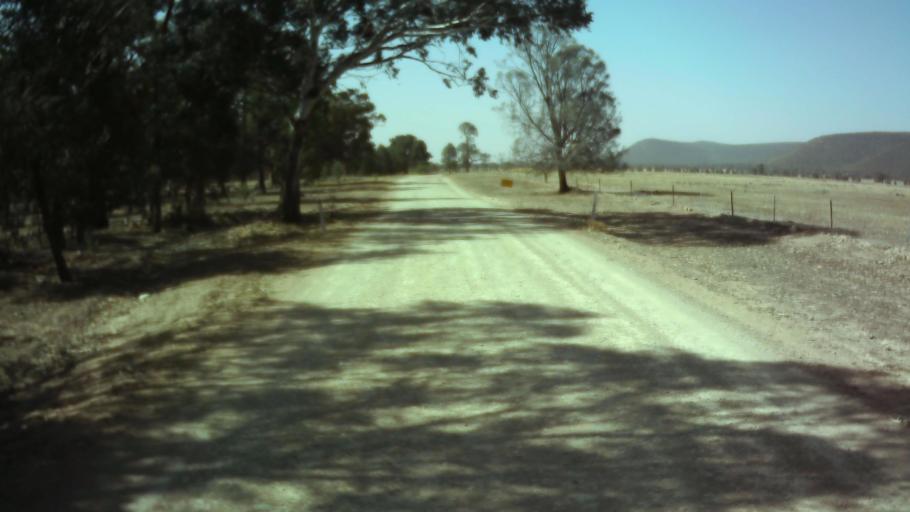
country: AU
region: New South Wales
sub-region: Weddin
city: Grenfell
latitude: -33.9467
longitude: 147.9282
